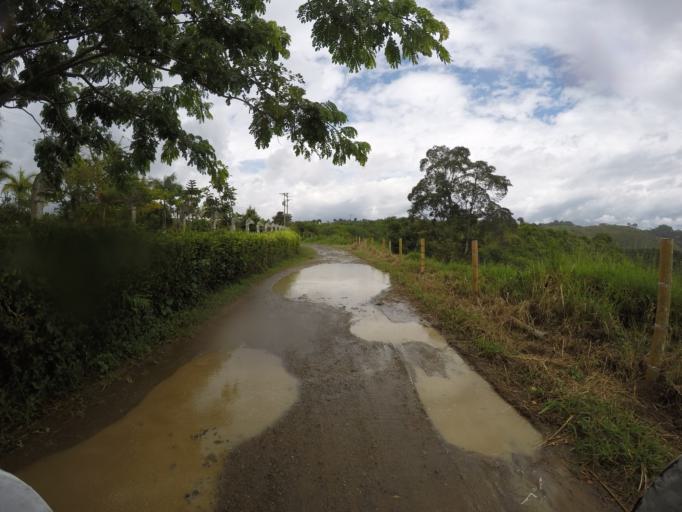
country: CO
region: Valle del Cauca
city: Ulloa
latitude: 4.6834
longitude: -75.7129
